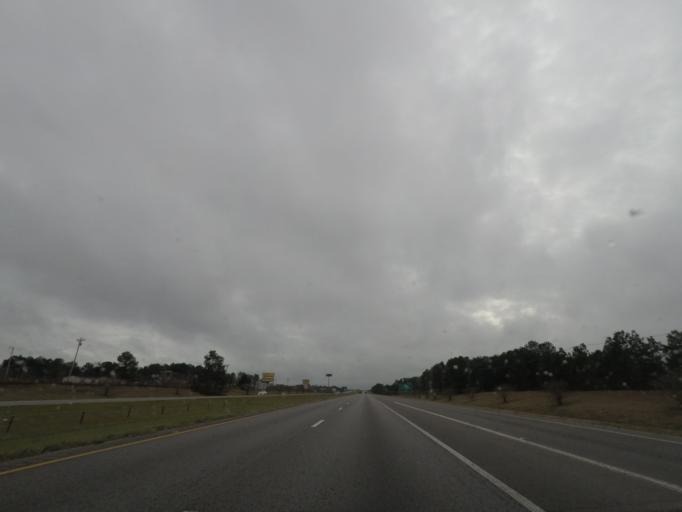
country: US
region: South Carolina
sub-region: Orangeburg County
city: Holly Hill
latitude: 33.4825
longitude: -80.4725
